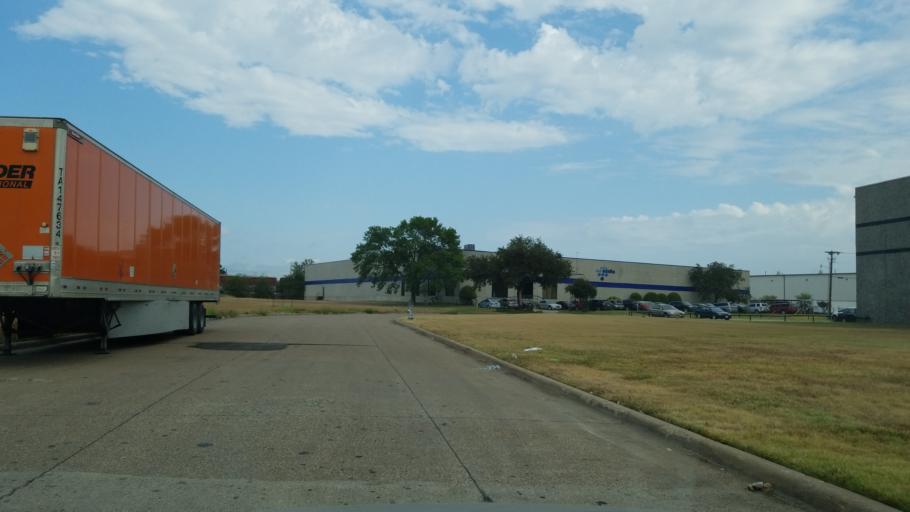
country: US
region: Texas
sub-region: Dallas County
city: Garland
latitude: 32.9026
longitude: -96.6907
